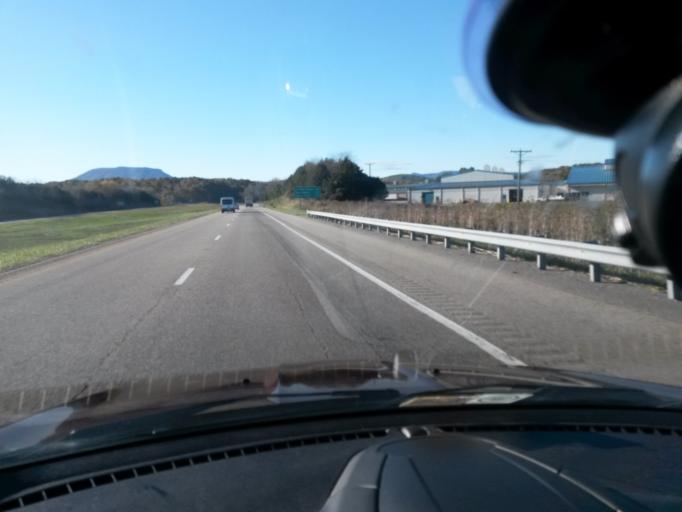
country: US
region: Virginia
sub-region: Rockbridge County
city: East Lexington
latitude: 37.8060
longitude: -79.4259
